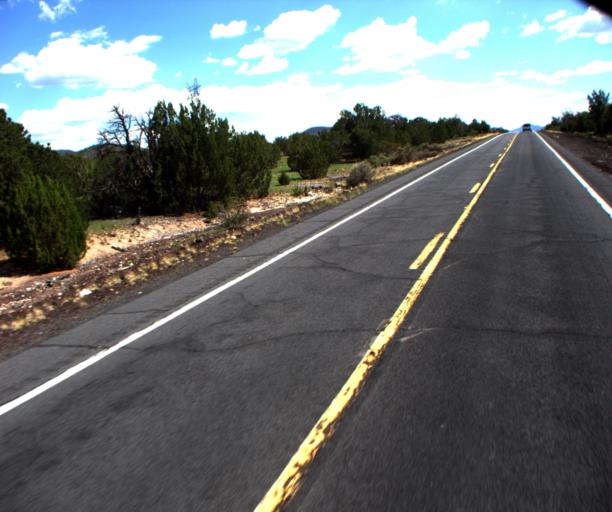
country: US
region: Arizona
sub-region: Coconino County
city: Williams
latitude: 35.4520
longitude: -112.1708
